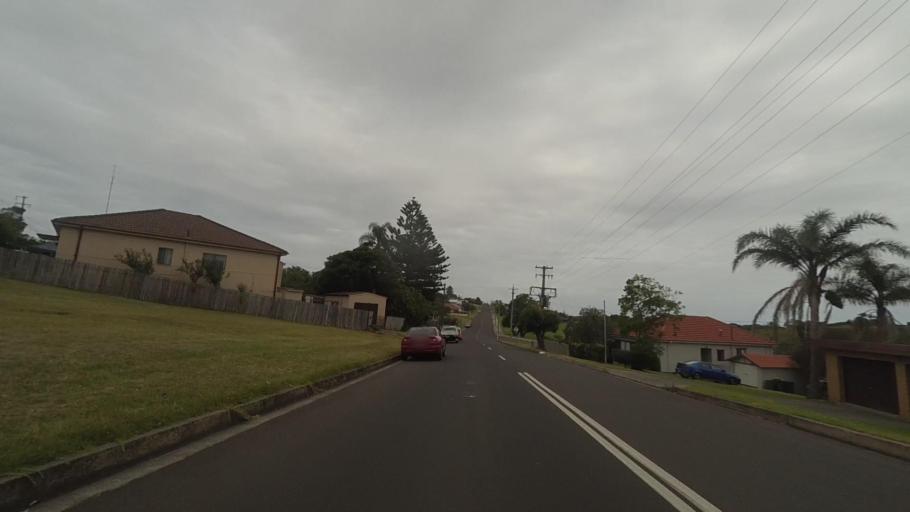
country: AU
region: New South Wales
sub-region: Wollongong
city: Port Kembla
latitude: -34.4874
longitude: 150.8993
